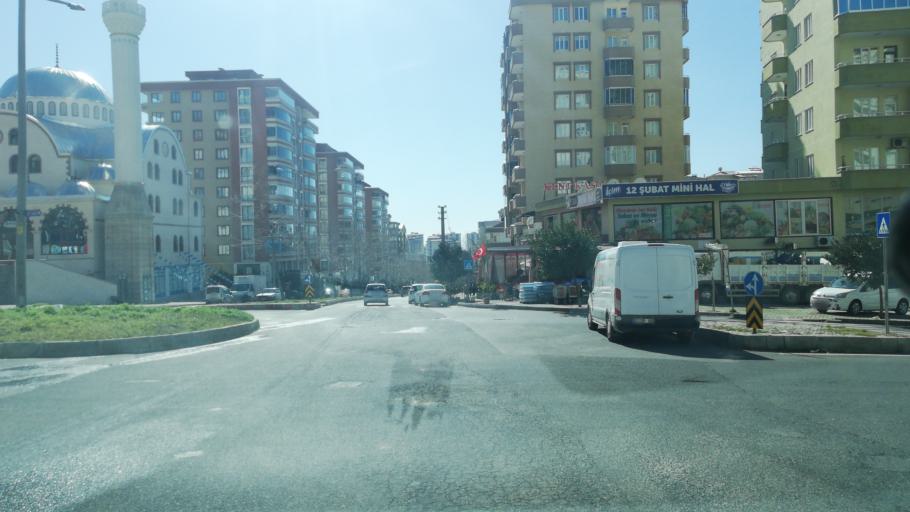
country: TR
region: Kahramanmaras
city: Kahramanmaras
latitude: 37.5871
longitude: 36.8785
